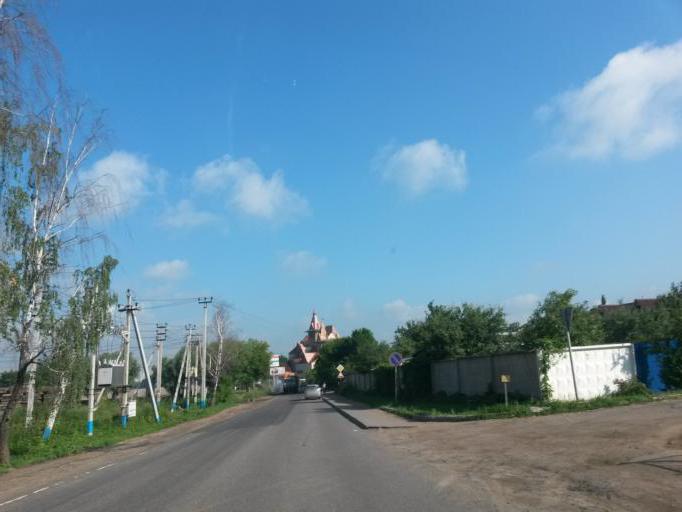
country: RU
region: Moscow
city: Zyablikovo
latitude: 55.6091
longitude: 37.7864
